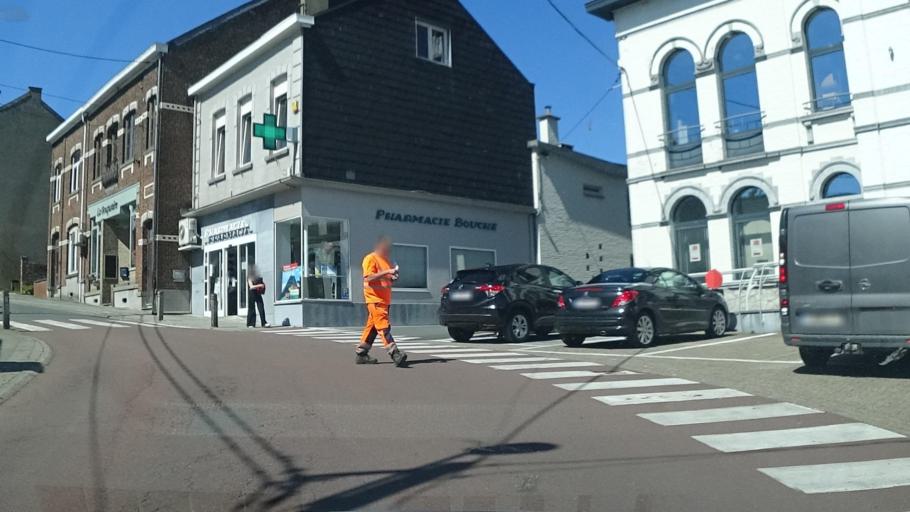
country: BE
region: Wallonia
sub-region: Province du Brabant Wallon
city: Mont-Saint-Guibert
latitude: 50.6367
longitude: 4.6121
